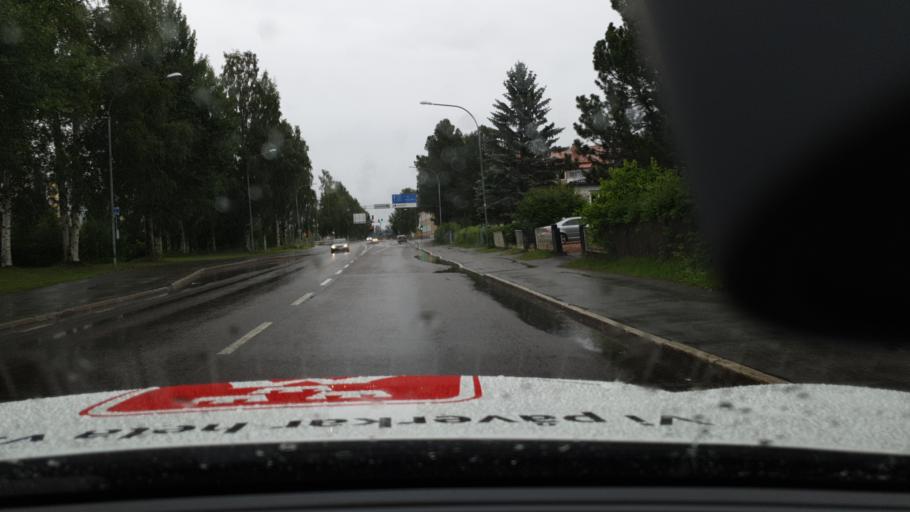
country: SE
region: Norrbotten
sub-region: Bodens Kommun
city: Boden
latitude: 65.8219
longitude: 21.6867
